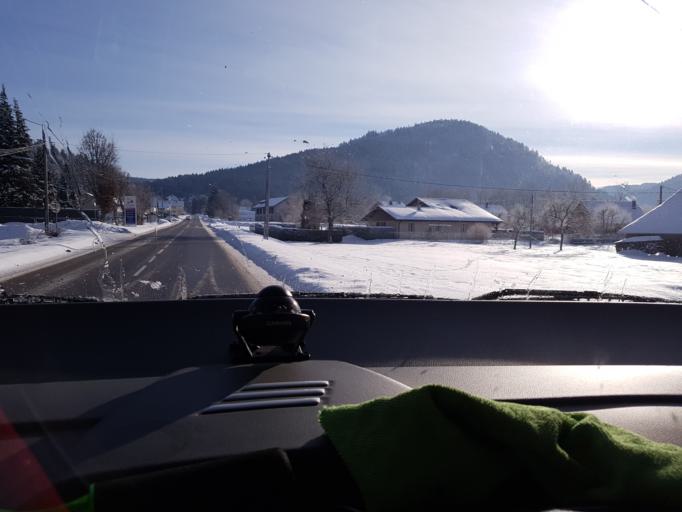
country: FR
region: Lorraine
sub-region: Departement des Vosges
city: Xonrupt-Longemer
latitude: 48.0835
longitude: 6.9383
